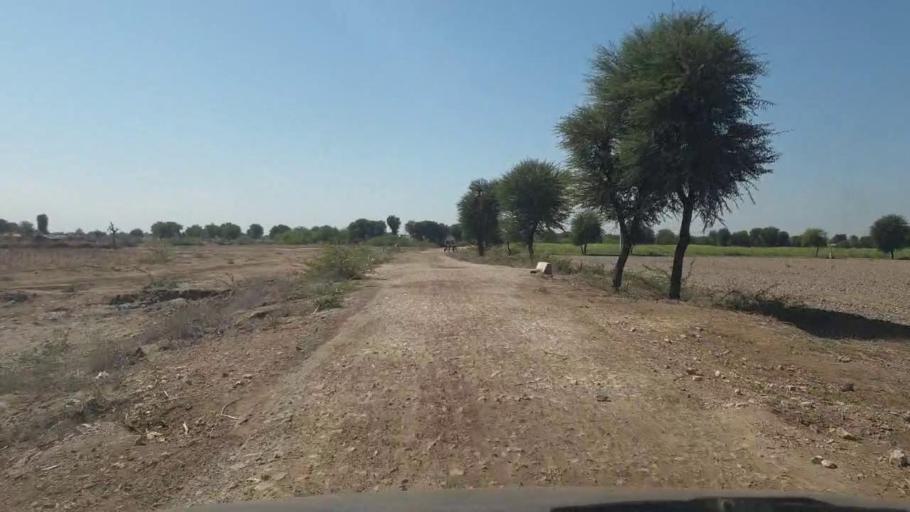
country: PK
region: Sindh
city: Umarkot
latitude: 25.3952
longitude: 69.6304
